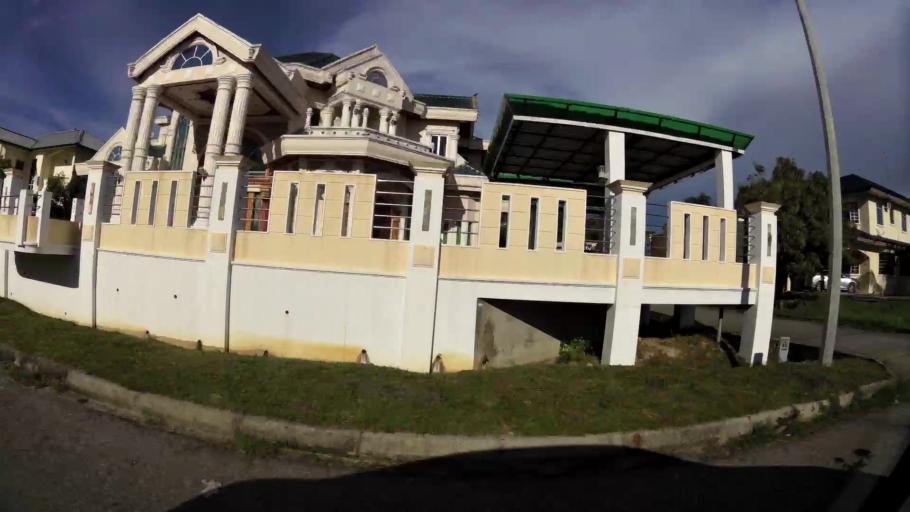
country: BN
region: Brunei and Muara
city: Bandar Seri Begawan
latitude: 4.9829
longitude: 114.9624
